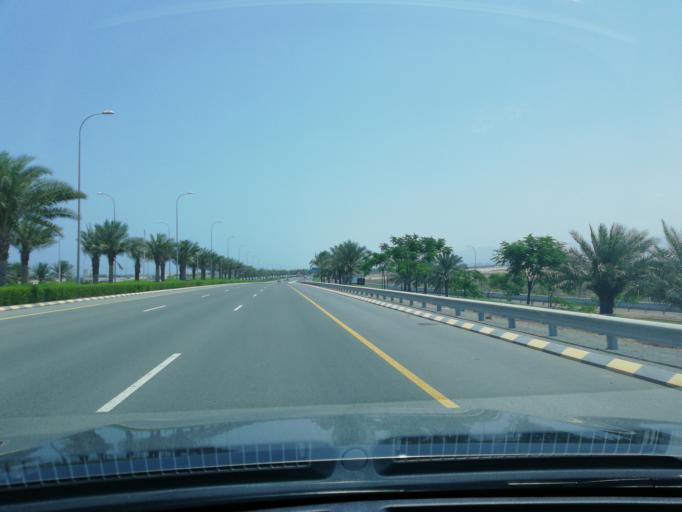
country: OM
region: Muhafazat Masqat
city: Bawshar
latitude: 23.6031
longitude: 58.3143
